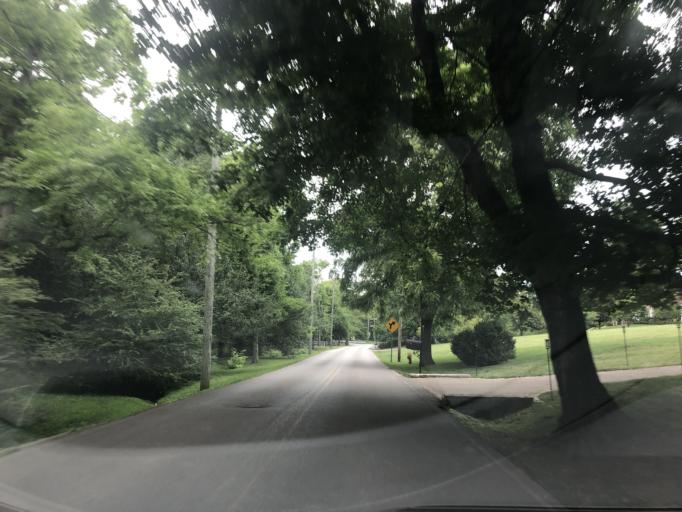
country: US
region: Tennessee
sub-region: Davidson County
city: Oak Hill
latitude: 36.0927
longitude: -86.7781
